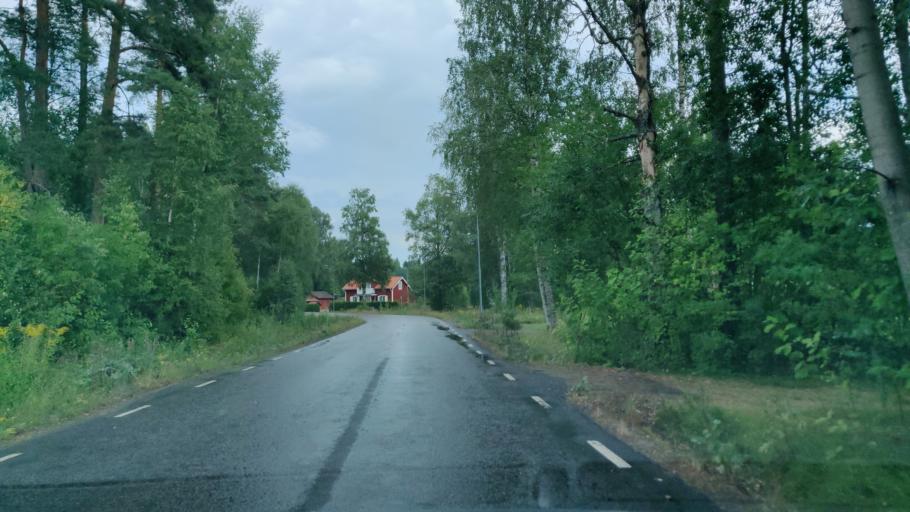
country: SE
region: Vaermland
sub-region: Munkfors Kommun
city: Munkfors
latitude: 59.8514
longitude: 13.5515
